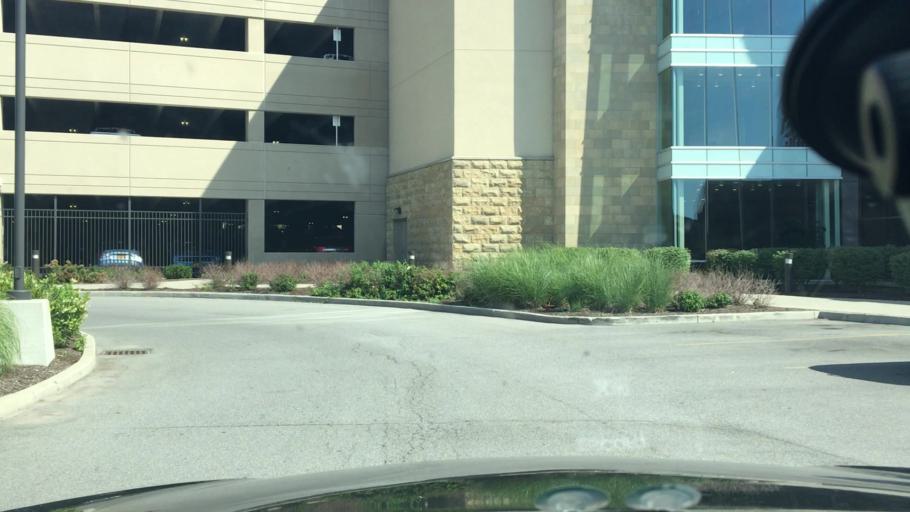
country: US
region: New York
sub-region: Erie County
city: Buffalo
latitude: 42.8742
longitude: -78.8700
